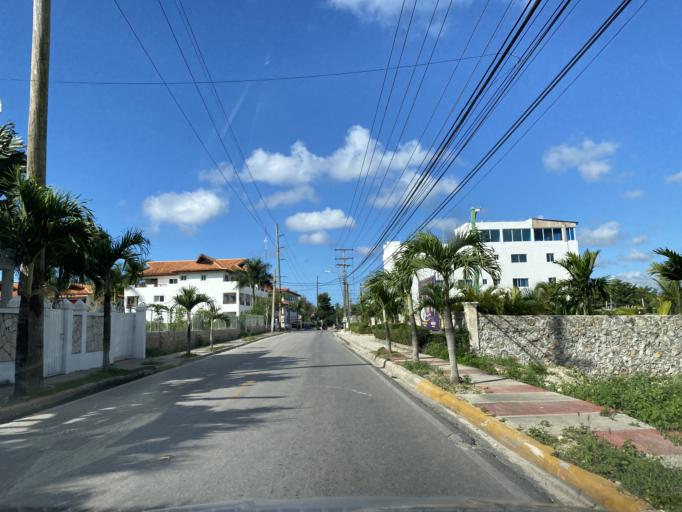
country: DO
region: La Romana
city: La Romana
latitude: 18.3702
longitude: -68.8361
